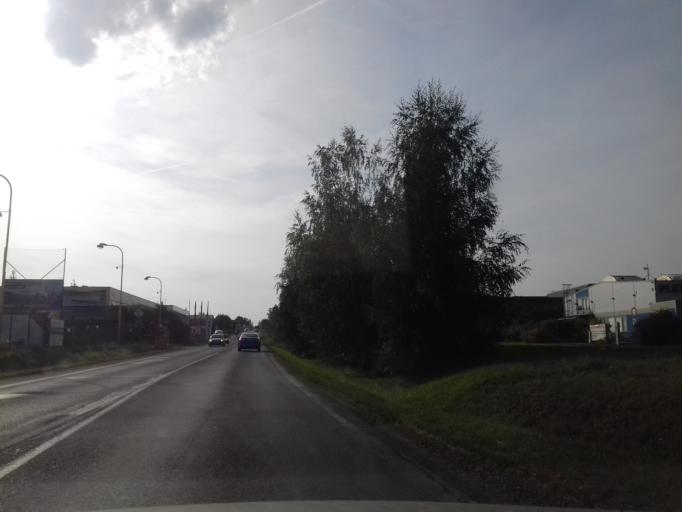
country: CZ
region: Central Bohemia
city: Vestec
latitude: 49.9891
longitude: 14.4916
